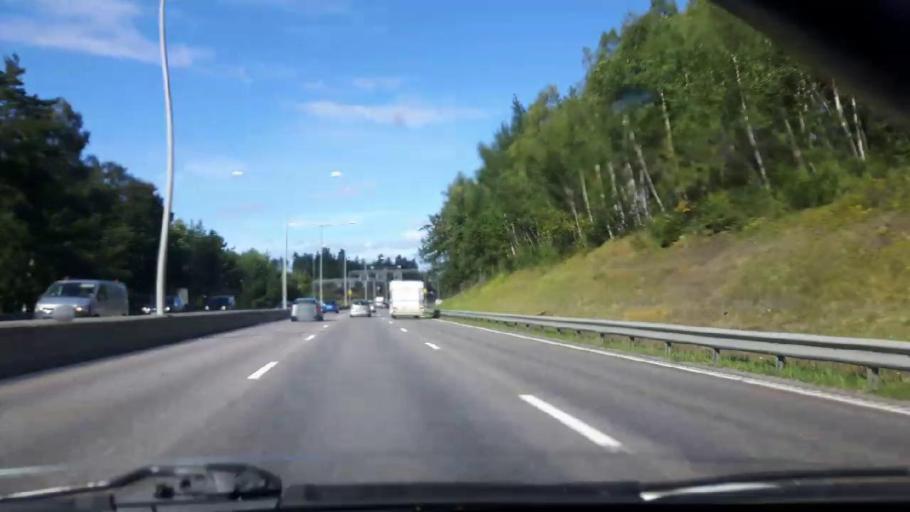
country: SE
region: Stockholm
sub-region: Botkyrka Kommun
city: Eriksberg
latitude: 59.2227
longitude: 17.7845
